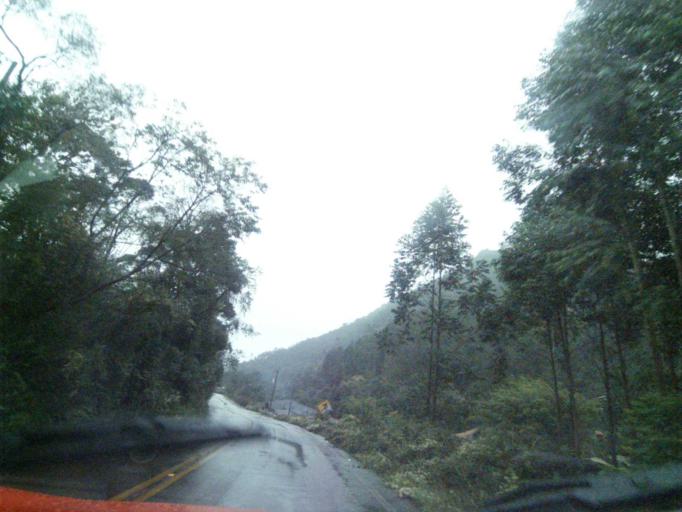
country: BR
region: Santa Catarina
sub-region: Anitapolis
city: Anitapolis
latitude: -27.8068
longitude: -49.0464
